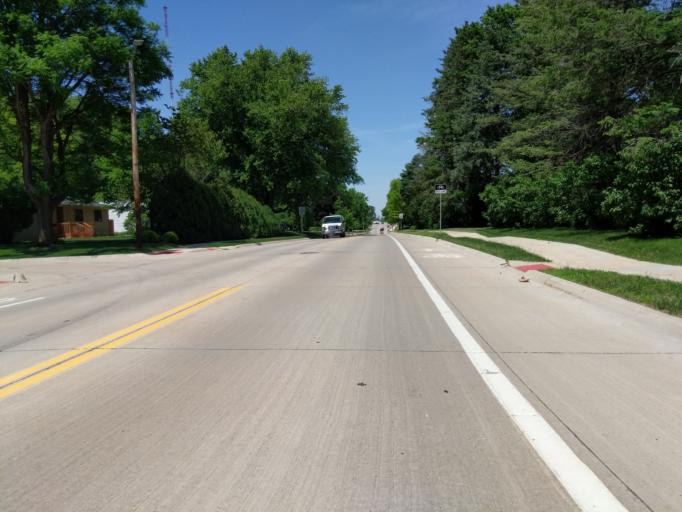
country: US
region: Iowa
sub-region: Linn County
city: Cedar Rapids
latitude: 42.0234
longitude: -91.6385
